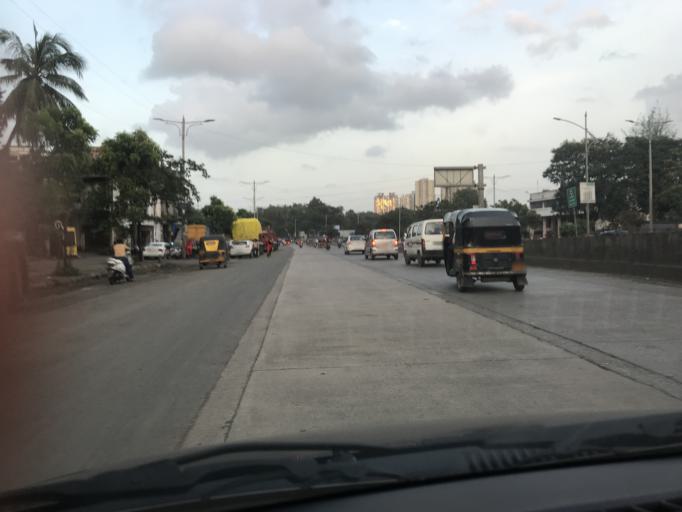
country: IN
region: Maharashtra
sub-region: Thane
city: Thane
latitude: 19.2181
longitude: 72.9817
